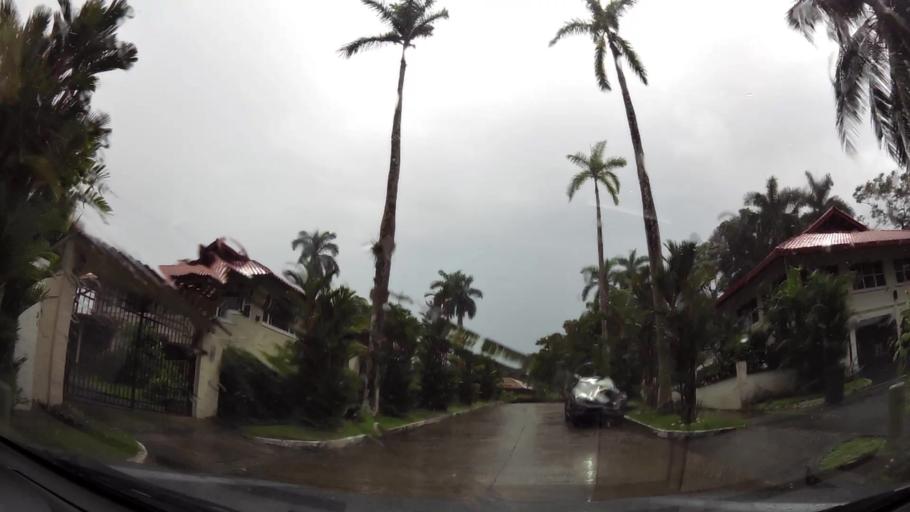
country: PA
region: Panama
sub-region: Distrito de Panama
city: Ancon
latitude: 8.9792
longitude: -79.5577
